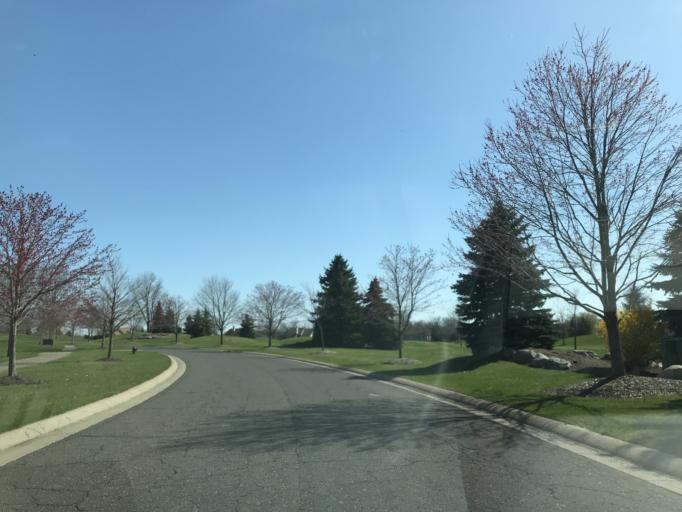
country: US
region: Michigan
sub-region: Oakland County
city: South Lyon
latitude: 42.4593
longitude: -83.5811
